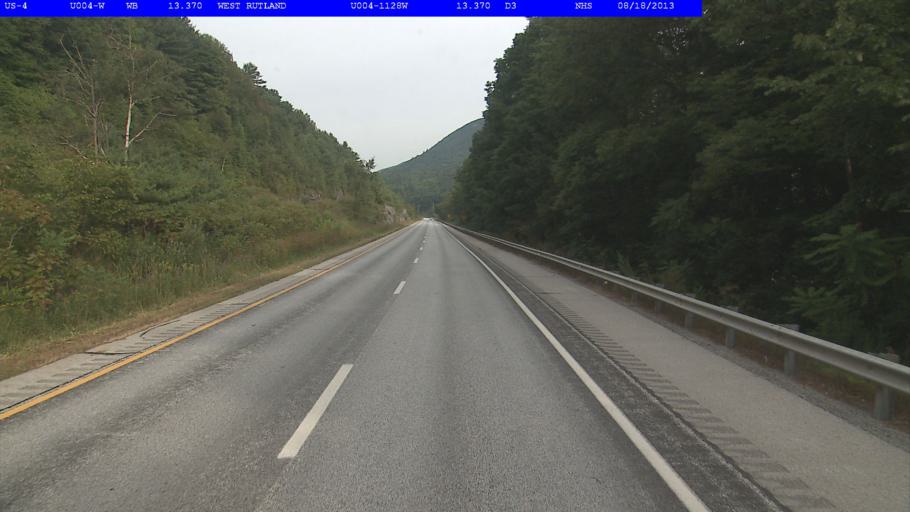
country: US
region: Vermont
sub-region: Rutland County
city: West Rutland
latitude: 43.6013
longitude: -73.0601
